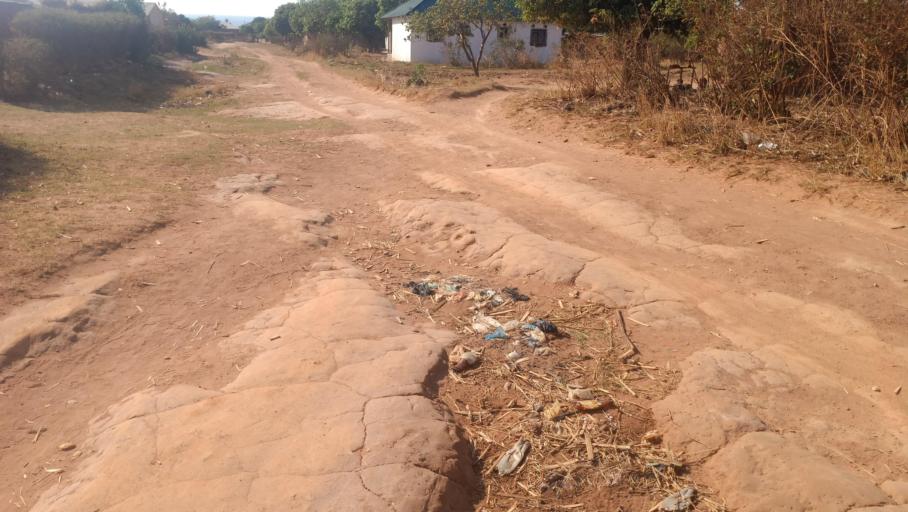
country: ZM
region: Northern
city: Mpika
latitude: -11.8274
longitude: 31.4565
